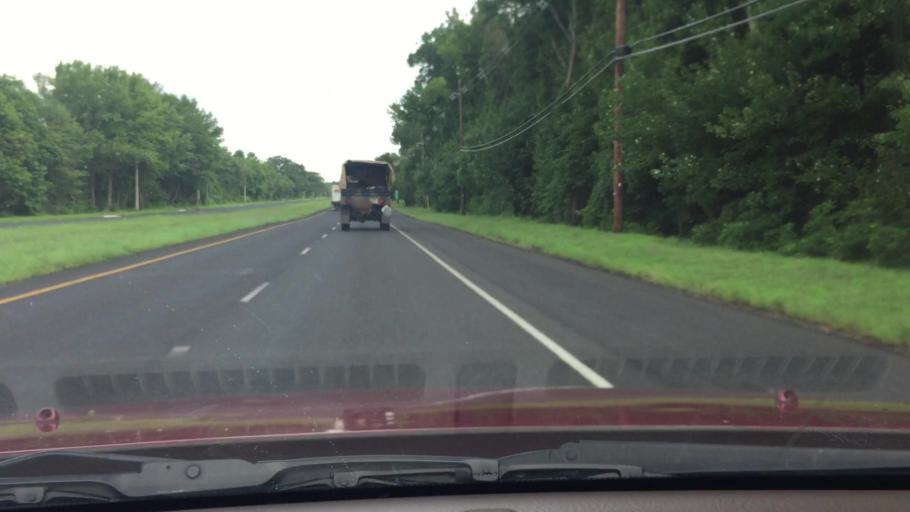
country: US
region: New Jersey
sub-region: Burlington County
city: Fort Dix
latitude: 40.0764
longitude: -74.6618
